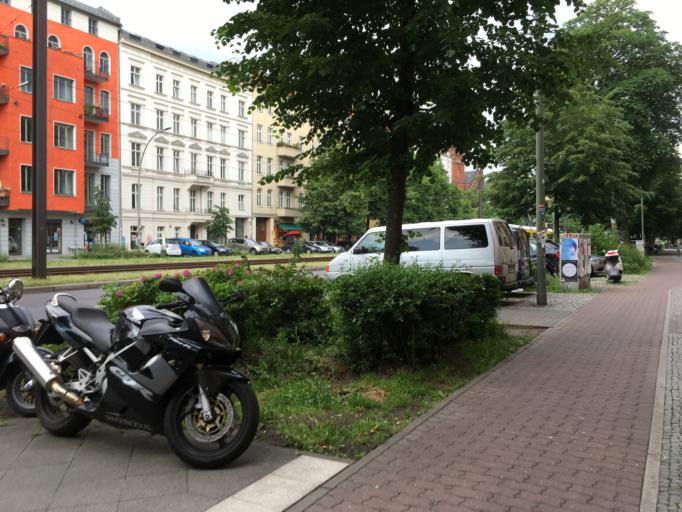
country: DE
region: Berlin
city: Prenzlauer Berg Bezirk
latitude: 52.5348
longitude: 13.4216
